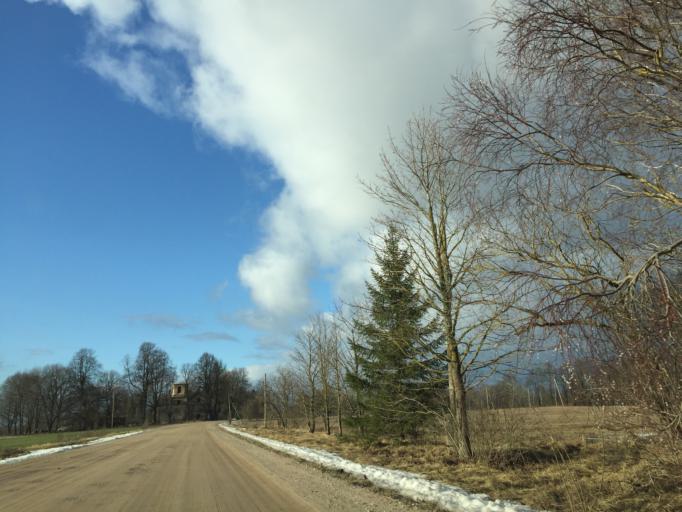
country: LV
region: Limbazu Rajons
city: Limbazi
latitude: 57.6162
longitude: 24.5816
